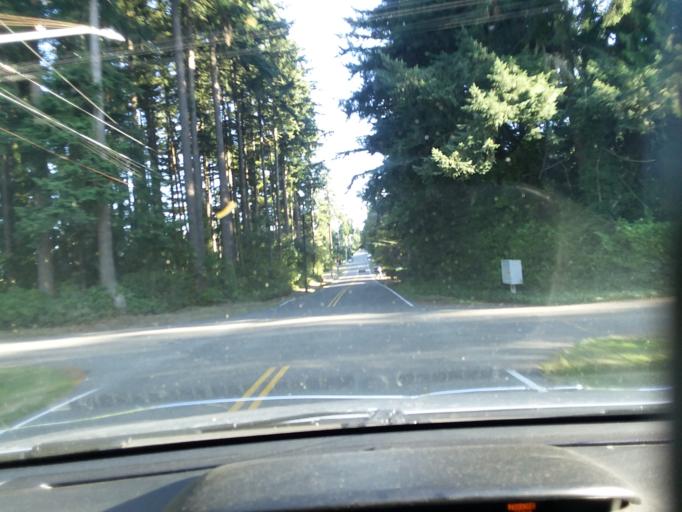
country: US
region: Washington
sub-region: Snohomish County
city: Esperance
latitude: 47.7980
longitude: -122.3411
